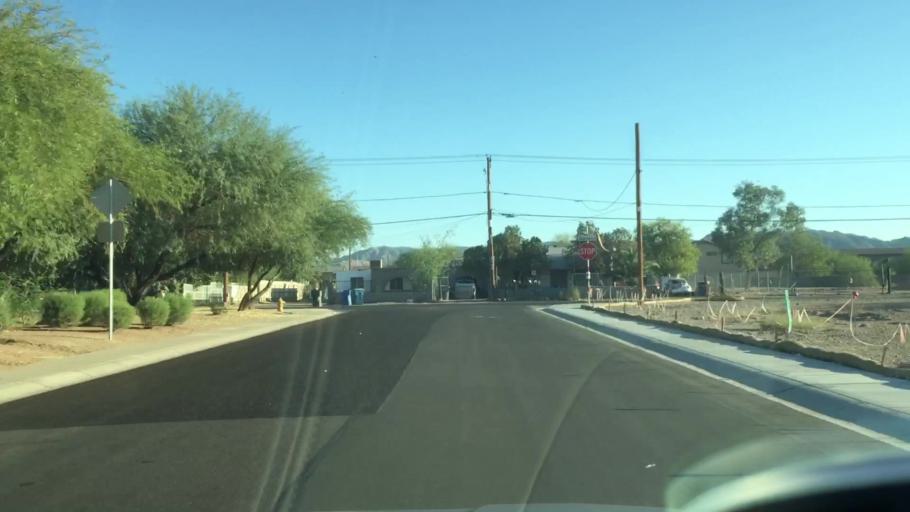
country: US
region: Arizona
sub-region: Maricopa County
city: Phoenix
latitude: 33.3964
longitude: -112.0851
